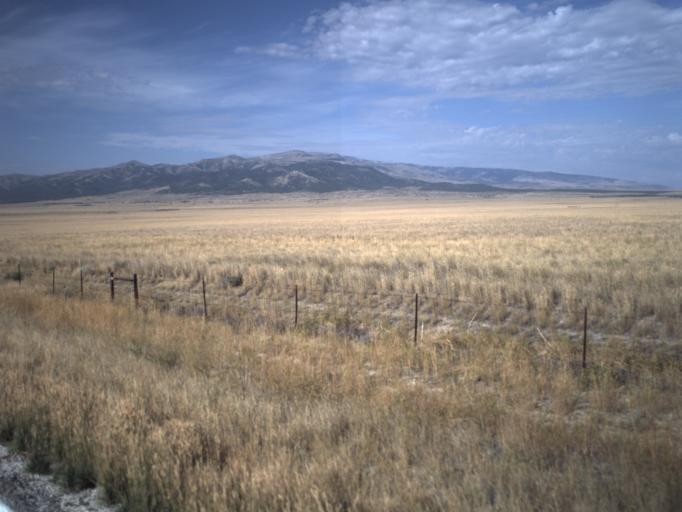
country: US
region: Idaho
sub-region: Oneida County
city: Malad City
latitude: 41.9614
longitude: -113.0652
